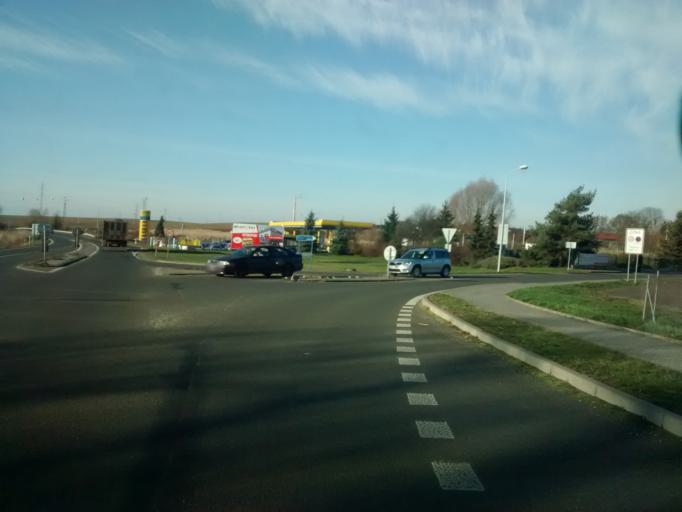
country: CZ
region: Central Bohemia
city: Dobrovice
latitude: 50.4106
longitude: 14.9764
